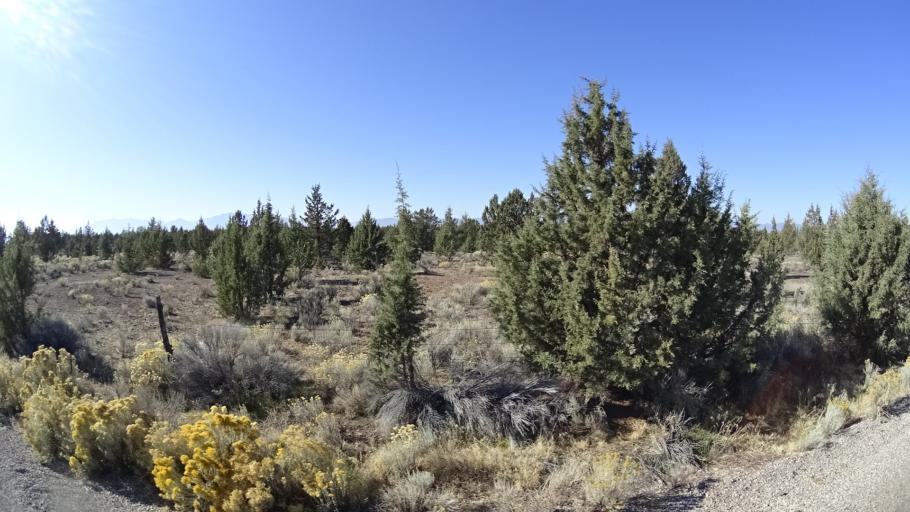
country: US
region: California
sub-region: Siskiyou County
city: Montague
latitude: 41.6375
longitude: -122.3403
